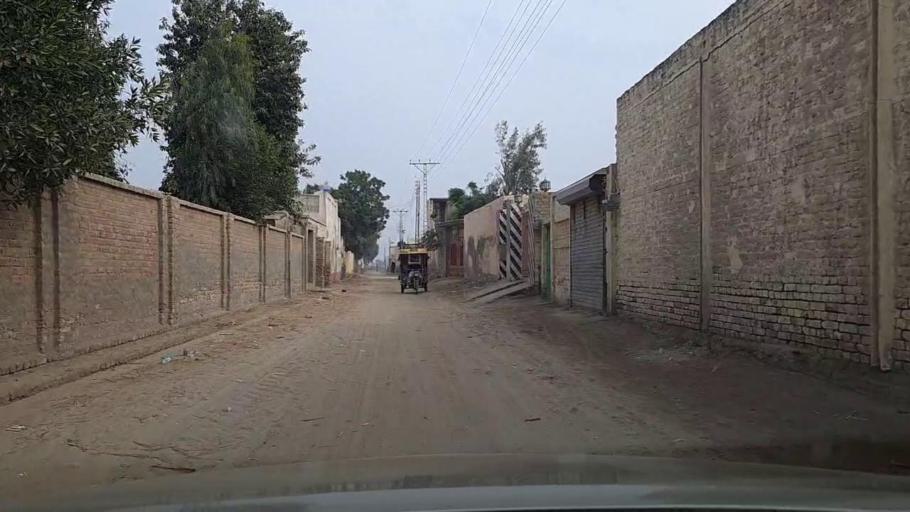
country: PK
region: Sindh
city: Sanghar
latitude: 26.1403
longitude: 68.9646
